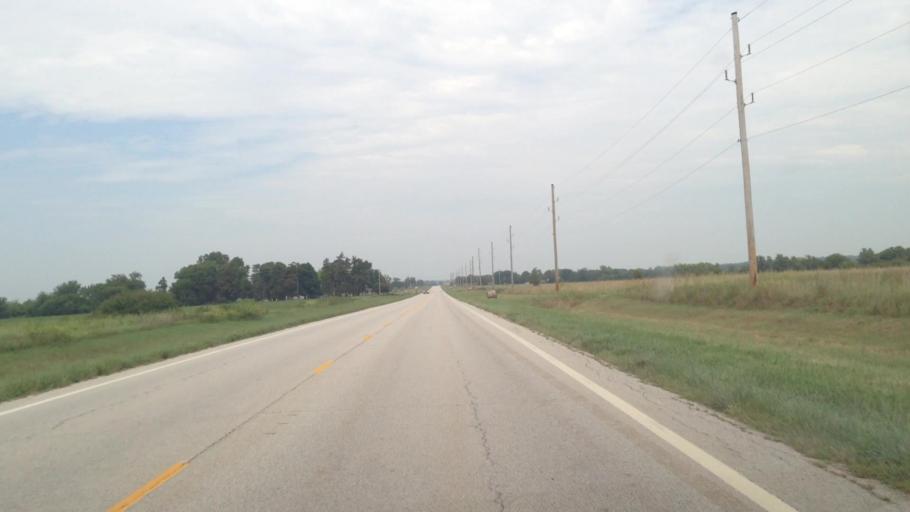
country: US
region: Kansas
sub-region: Allen County
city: Iola
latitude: 37.9755
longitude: -95.1703
